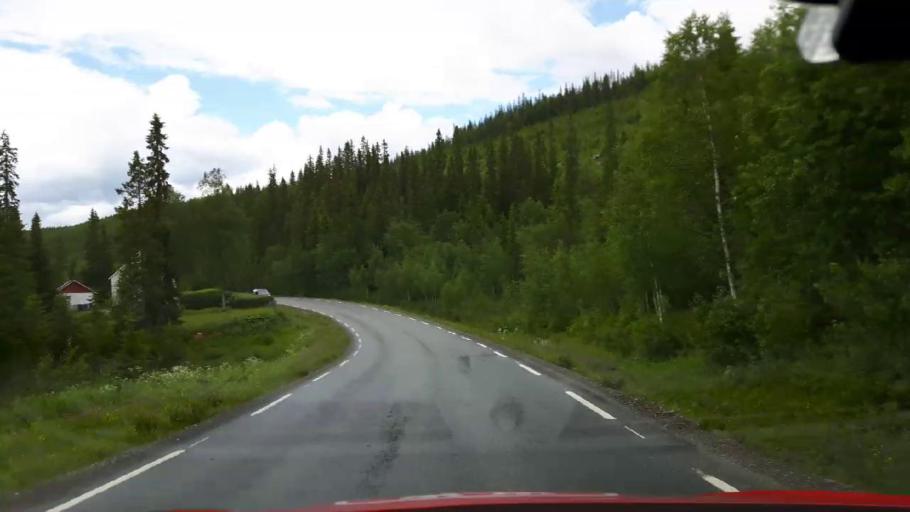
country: NO
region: Nord-Trondelag
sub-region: Lierne
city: Sandvika
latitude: 64.1140
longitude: 13.9701
